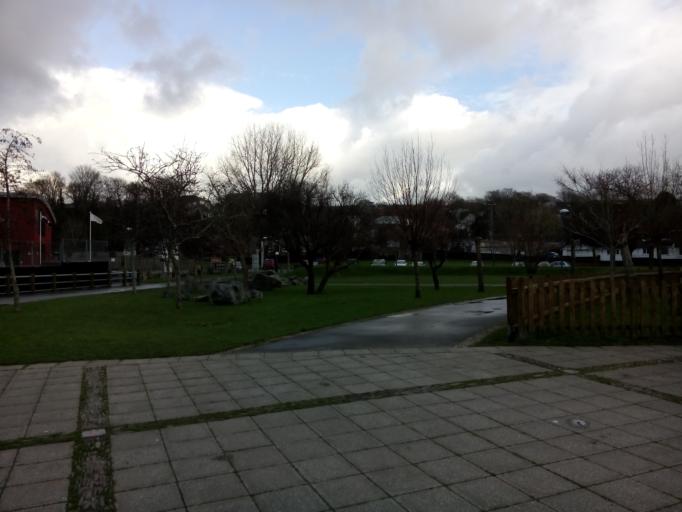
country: GB
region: England
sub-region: Cornwall
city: Helston
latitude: 50.0990
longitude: -5.2800
